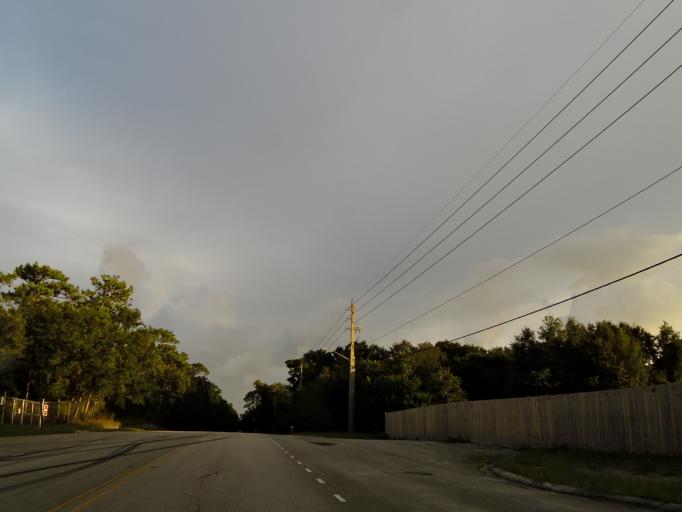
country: US
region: Florida
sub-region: Duval County
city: Atlantic Beach
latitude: 30.3712
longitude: -81.4867
